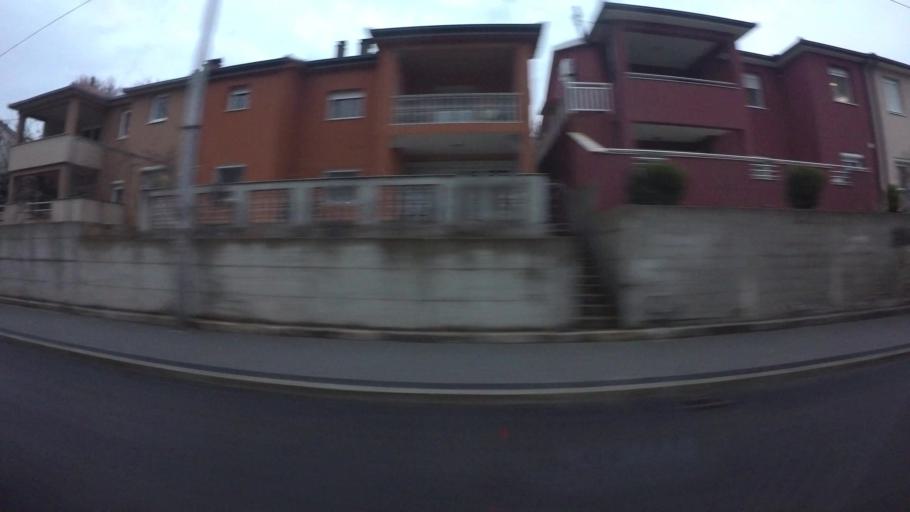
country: BA
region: Federation of Bosnia and Herzegovina
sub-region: Hercegovacko-Bosanski Kanton
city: Mostar
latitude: 43.3523
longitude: 17.8123
